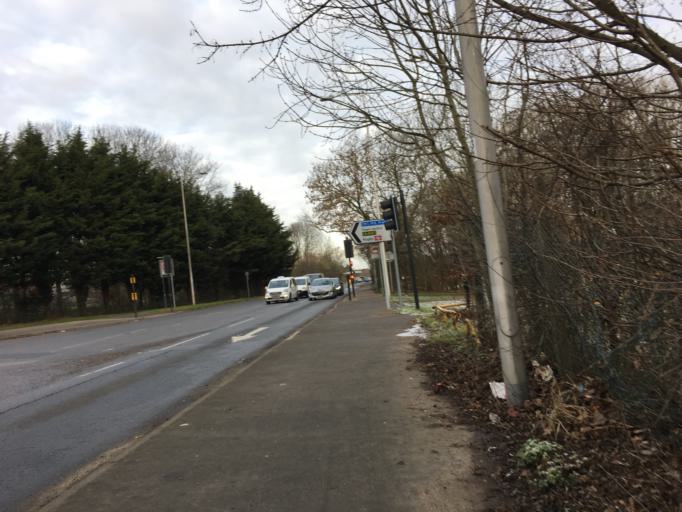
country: GB
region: England
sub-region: Warwickshire
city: Rugby
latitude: 52.3828
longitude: -1.2470
